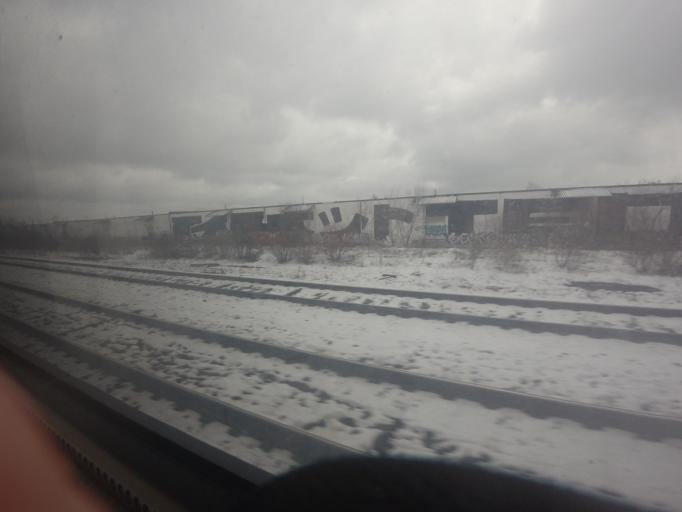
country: CA
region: Ontario
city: Scarborough
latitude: 43.7272
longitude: -79.2482
